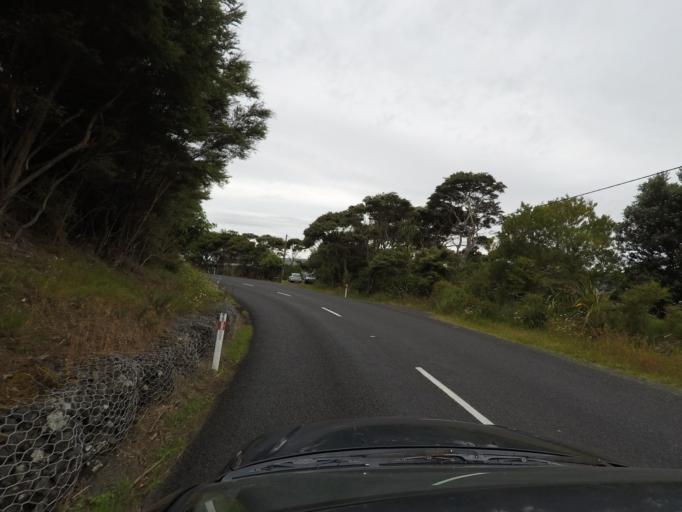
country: NZ
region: Waikato
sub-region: Waikato District
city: Raglan
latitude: -37.8242
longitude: 174.8149
